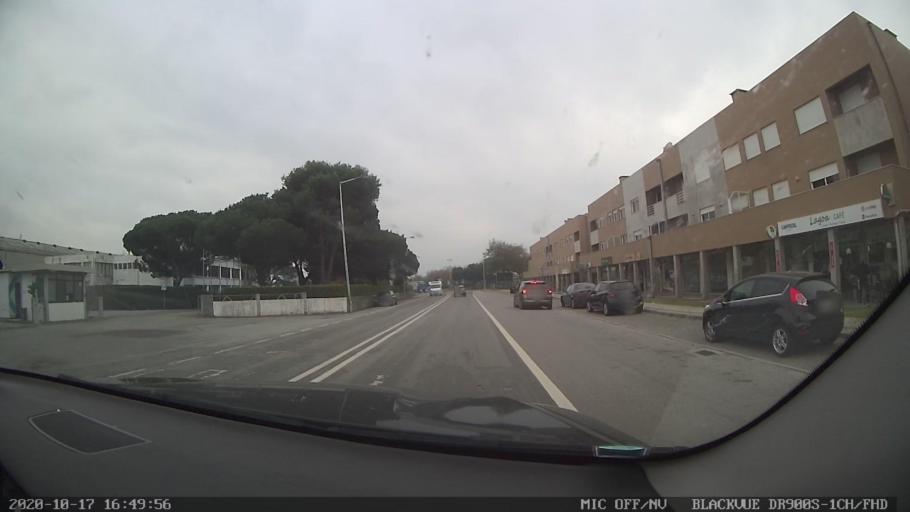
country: PT
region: Braga
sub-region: Esposende
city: Esposende
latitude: 41.5270
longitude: -8.7765
